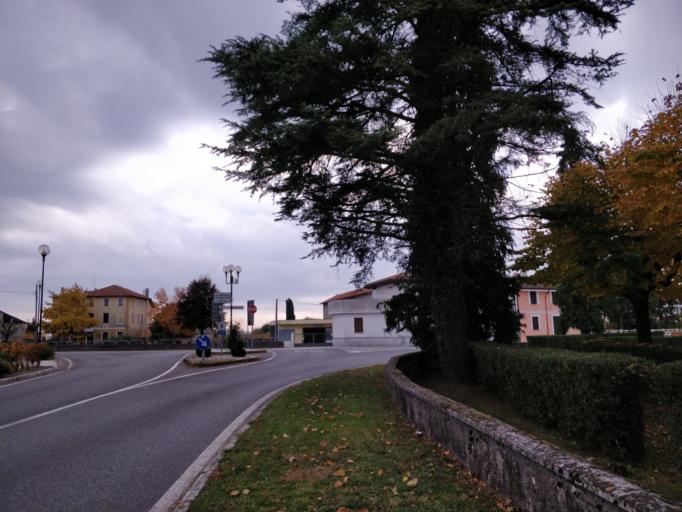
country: IT
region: Friuli Venezia Giulia
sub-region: Provincia di Udine
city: Bertiolo
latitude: 45.9439
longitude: 13.0557
